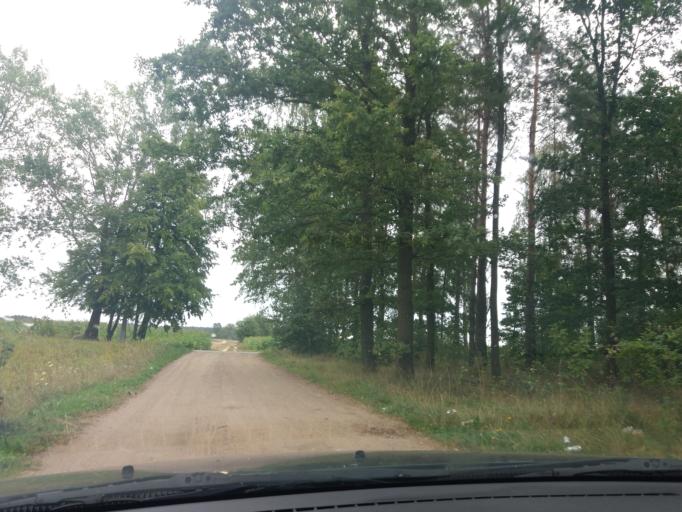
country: PL
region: Masovian Voivodeship
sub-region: Powiat mlawski
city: Wieczfnia Koscielna
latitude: 53.2341
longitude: 20.4895
